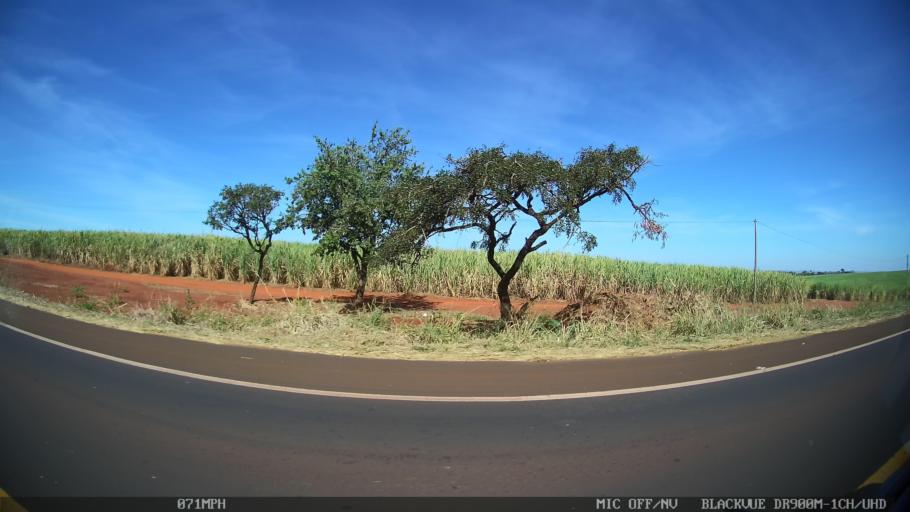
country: BR
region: Sao Paulo
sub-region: Franca
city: Franca
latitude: -20.5583
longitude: -47.5989
